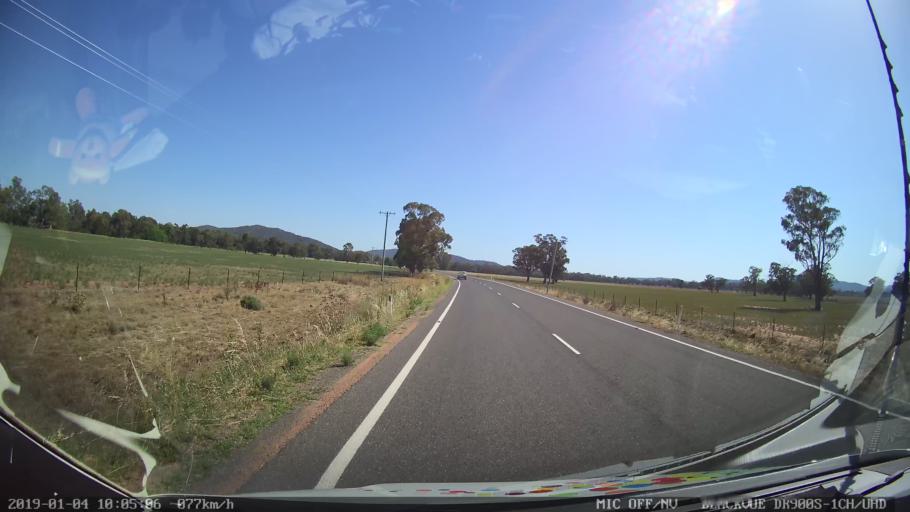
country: AU
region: New South Wales
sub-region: Cabonne
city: Canowindra
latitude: -33.4456
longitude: 148.3640
